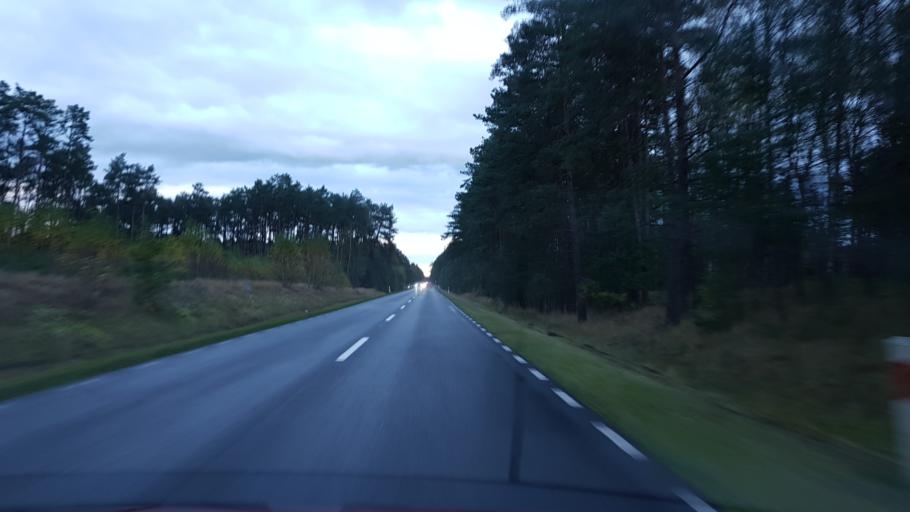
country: PL
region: Greater Poland Voivodeship
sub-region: Powiat pilski
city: Smilowo
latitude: 53.2069
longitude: 16.8475
